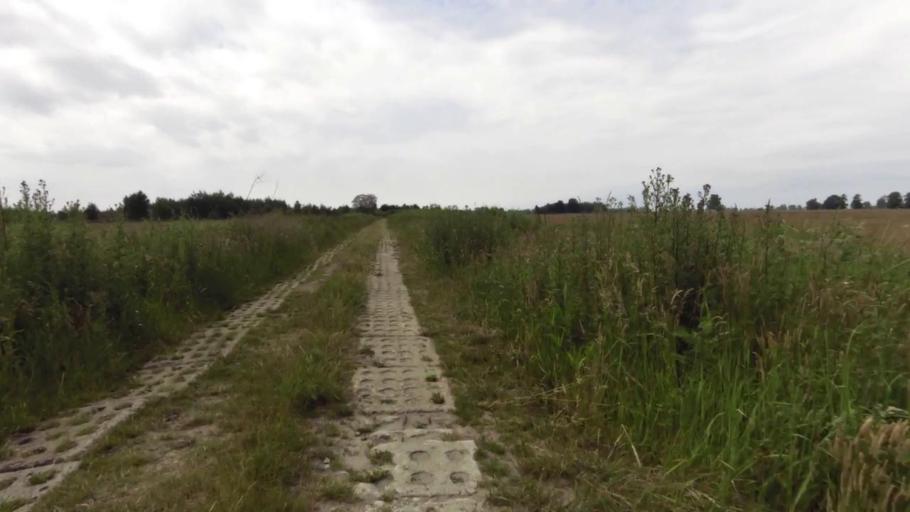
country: PL
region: West Pomeranian Voivodeship
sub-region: Powiat goleniowski
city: Stepnica
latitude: 53.7148
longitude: 14.5851
